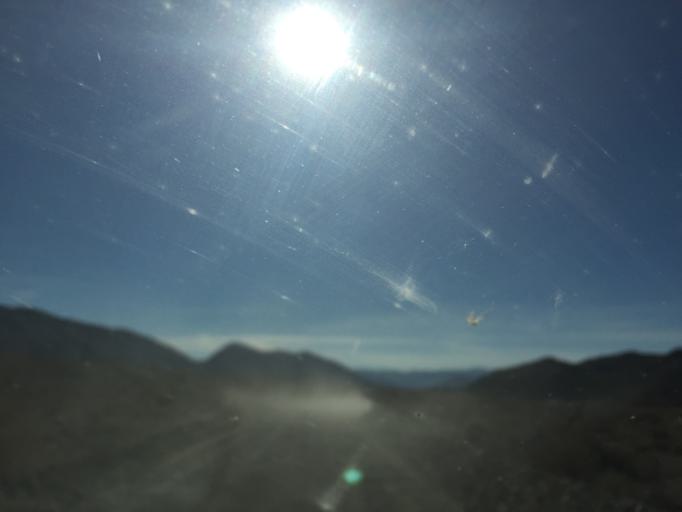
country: US
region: California
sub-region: Inyo County
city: Lone Pine
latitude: 36.8027
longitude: -117.5139
